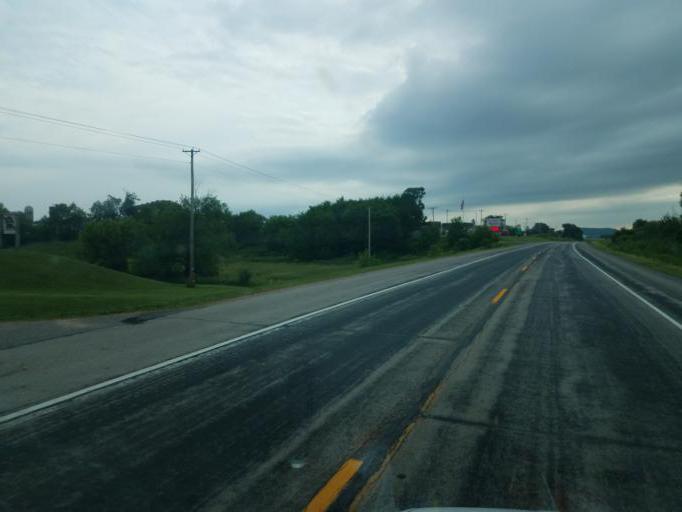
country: US
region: Wisconsin
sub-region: Vernon County
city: Hillsboro
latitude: 43.6592
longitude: -90.3295
